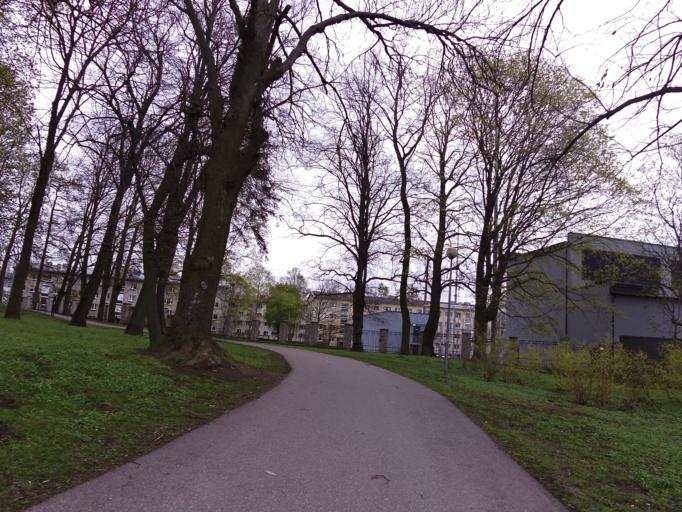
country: EE
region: Harju
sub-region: Tallinna linn
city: Tallinn
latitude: 59.4521
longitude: 24.6838
